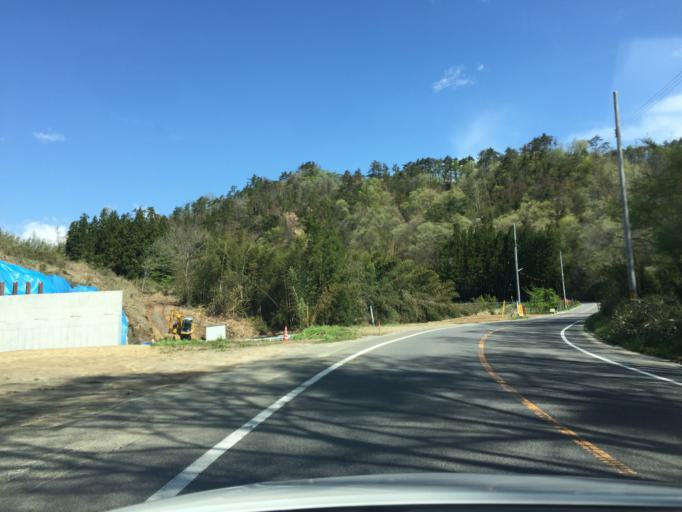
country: JP
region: Fukushima
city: Funehikimachi-funehiki
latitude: 37.5353
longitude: 140.5401
